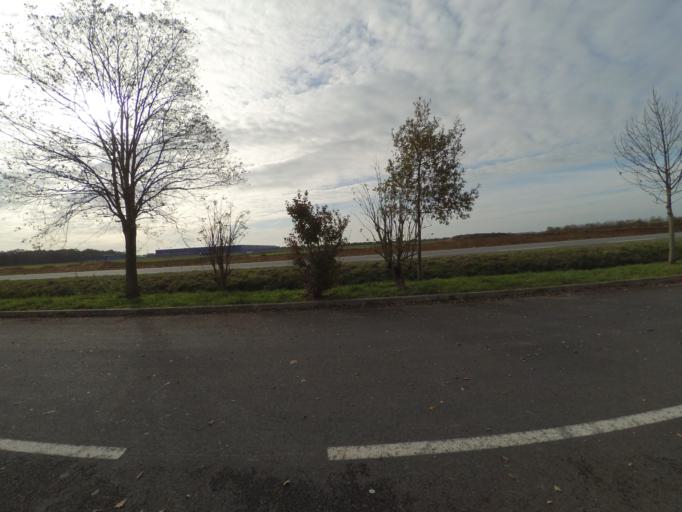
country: FR
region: Pays de la Loire
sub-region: Departement de la Vendee
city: Saint-Hilaire-de-Loulay
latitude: 47.0243
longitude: -1.3477
